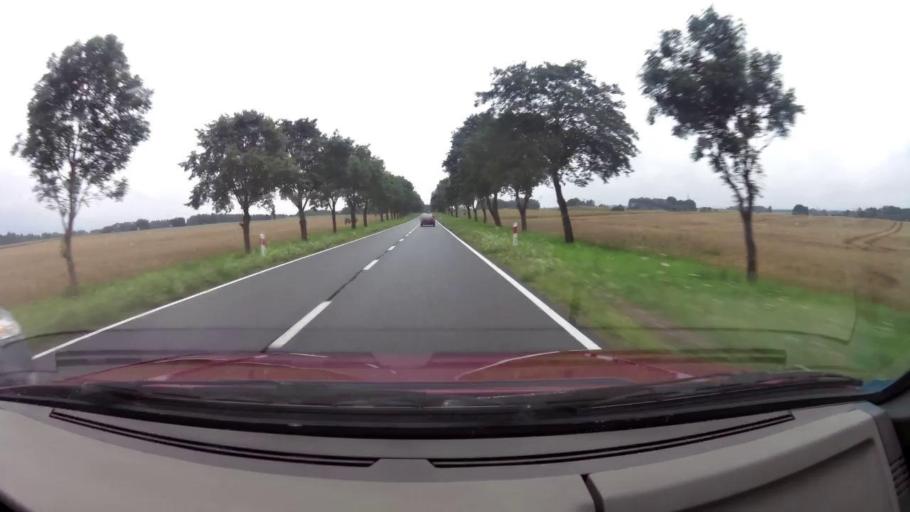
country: PL
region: West Pomeranian Voivodeship
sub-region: Powiat stargardzki
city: Chociwel
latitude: 53.4527
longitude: 15.3218
